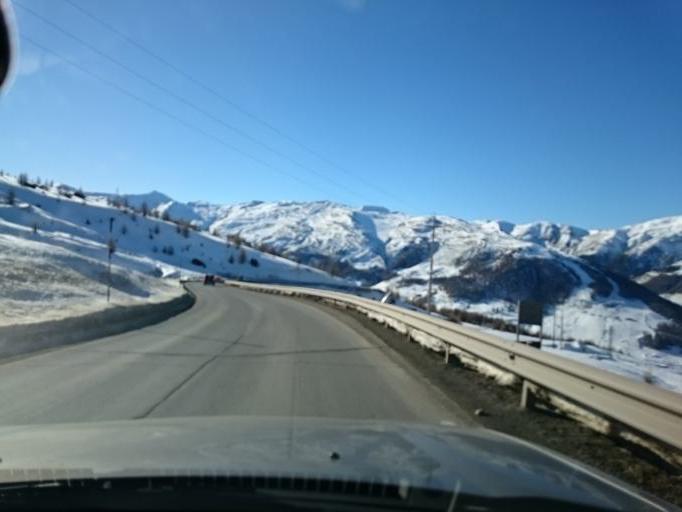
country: IT
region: Lombardy
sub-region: Provincia di Sondrio
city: Livigno
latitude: 46.5384
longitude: 10.1637
